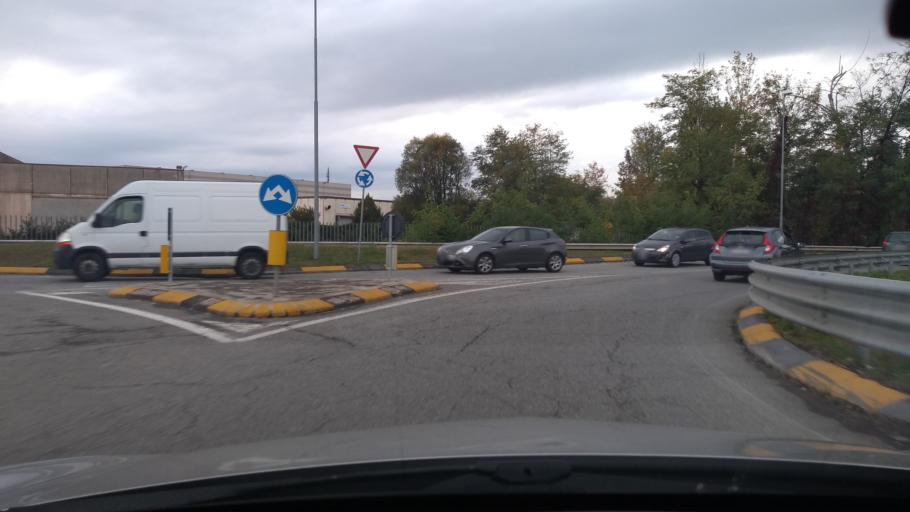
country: IT
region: Lombardy
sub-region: Provincia di Bergamo
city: Levate
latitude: 45.6166
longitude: 9.6334
